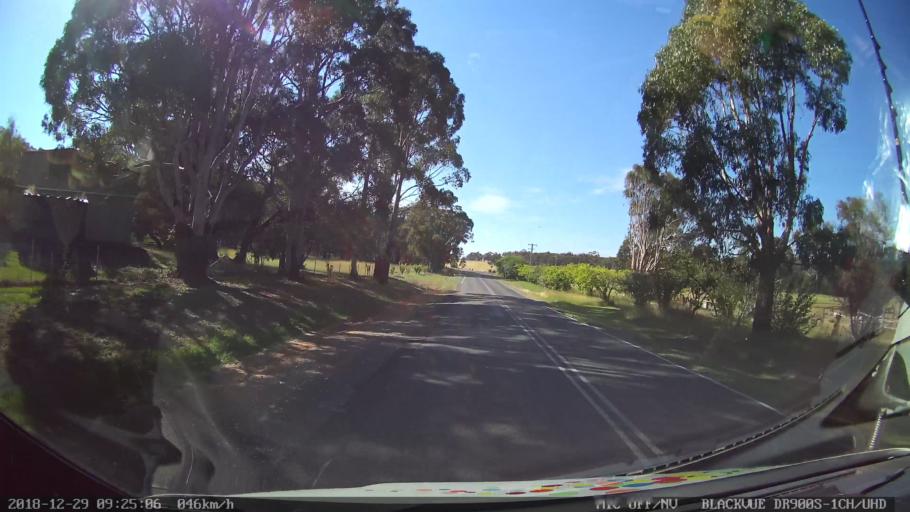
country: AU
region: New South Wales
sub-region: Upper Lachlan Shire
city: Crookwell
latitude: -34.5414
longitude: 149.3937
